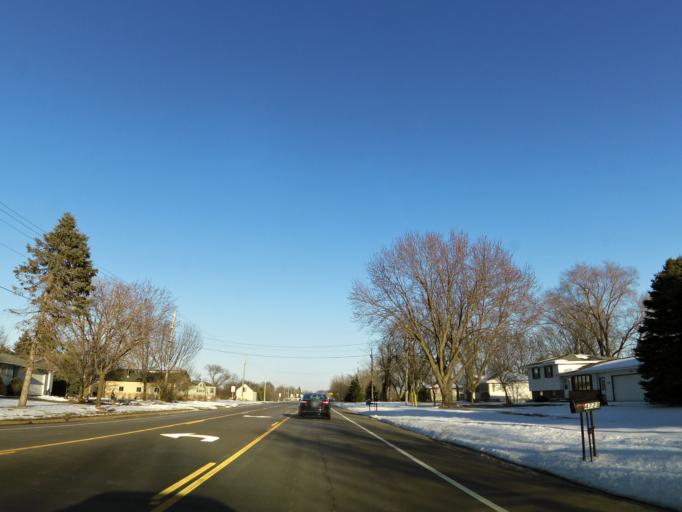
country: US
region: Minnesota
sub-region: Dakota County
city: Farmington
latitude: 44.6591
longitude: -93.0107
